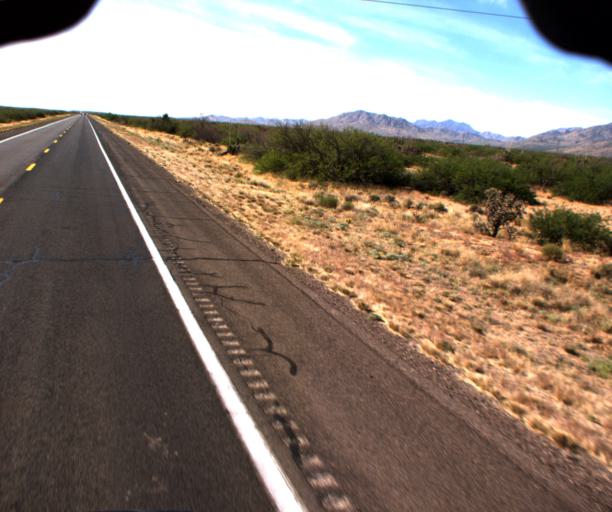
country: US
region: Arizona
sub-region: Graham County
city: Swift Trail Junction
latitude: 32.6728
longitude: -109.7041
